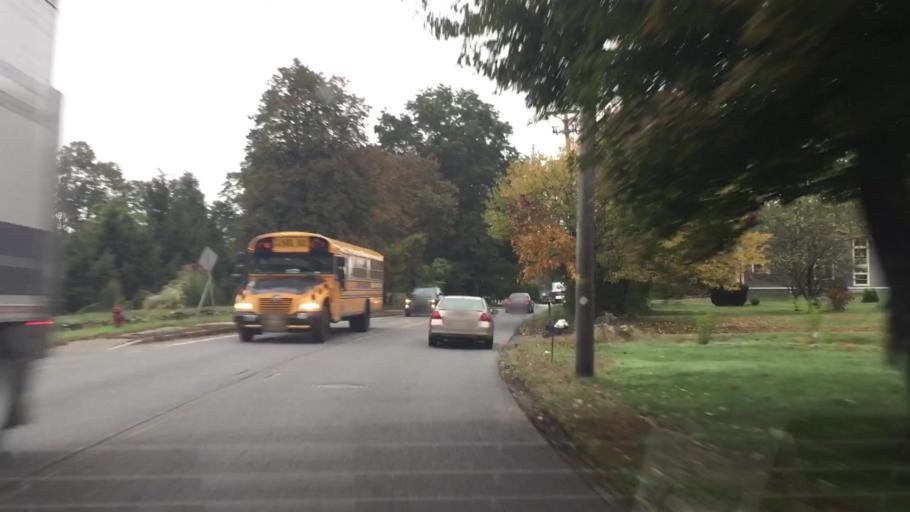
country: US
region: Massachusetts
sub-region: Essex County
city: Methuen
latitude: 42.7005
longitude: -71.2467
